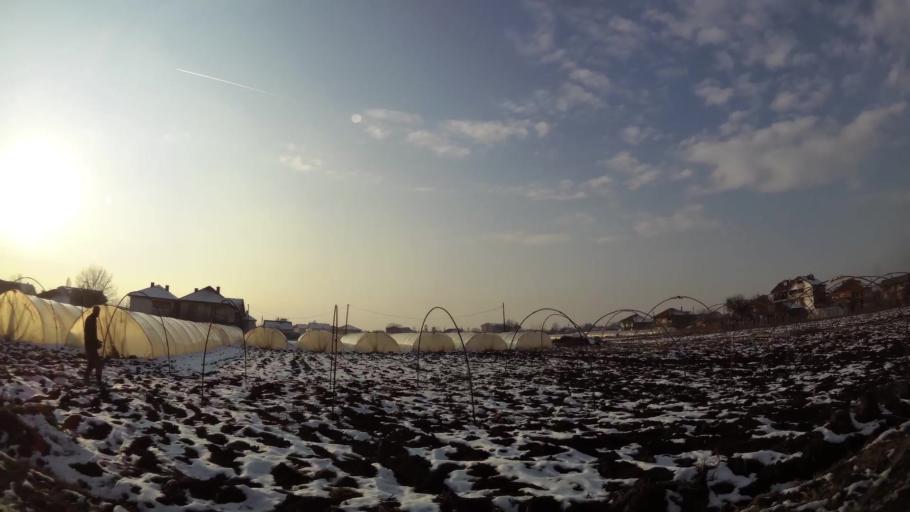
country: MK
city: Creshevo
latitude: 42.0251
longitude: 21.5197
